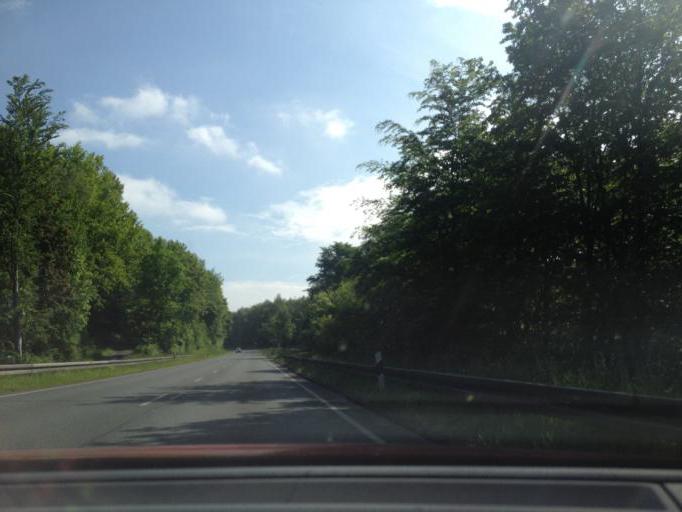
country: DE
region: Bavaria
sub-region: Upper Franconia
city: Arzberg
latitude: 50.0600
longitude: 12.1772
